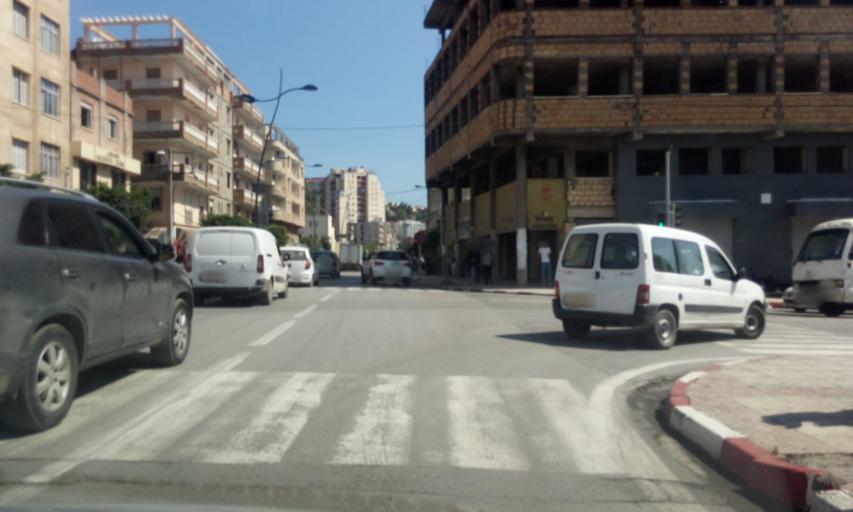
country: DZ
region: Bejaia
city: Bejaia
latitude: 36.7523
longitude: 5.0706
